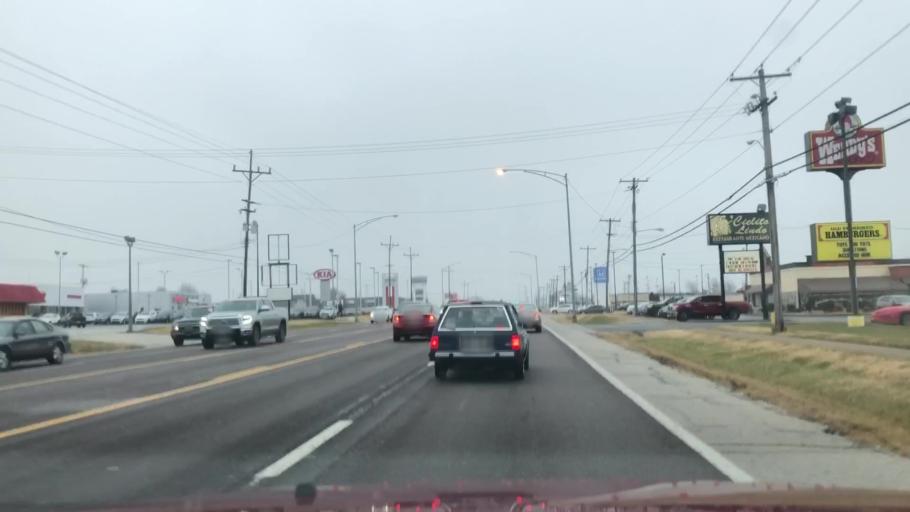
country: US
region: Missouri
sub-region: Greene County
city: Springfield
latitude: 37.1489
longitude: -93.2958
